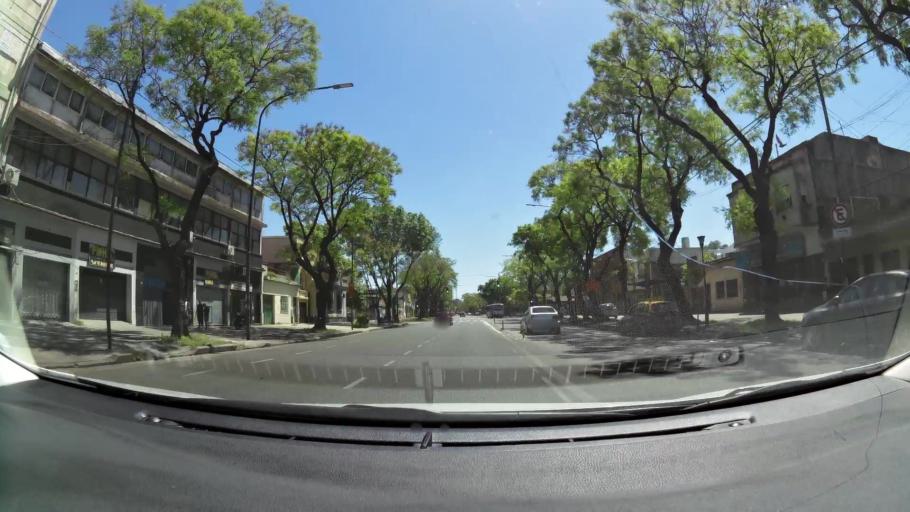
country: AR
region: Buenos Aires F.D.
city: Buenos Aires
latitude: -34.6452
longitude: -58.4143
